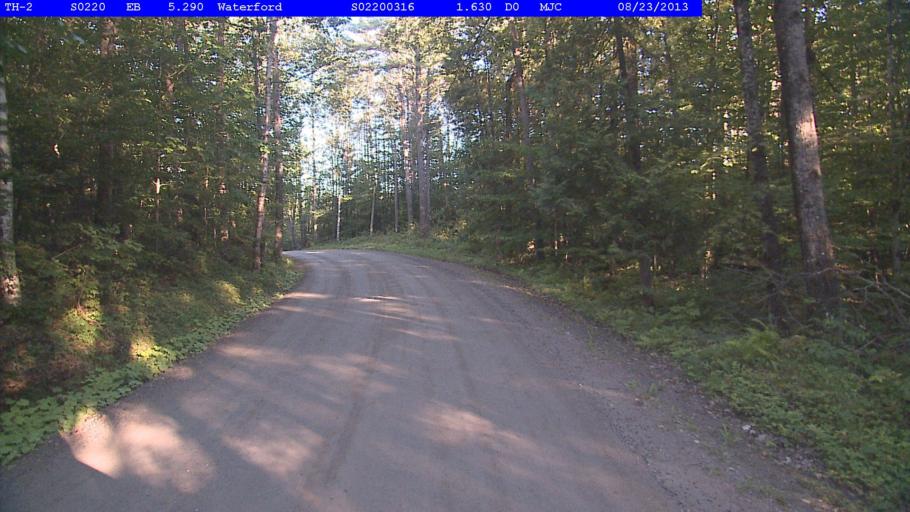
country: US
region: Vermont
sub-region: Caledonia County
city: Saint Johnsbury
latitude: 44.3394
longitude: -71.9693
